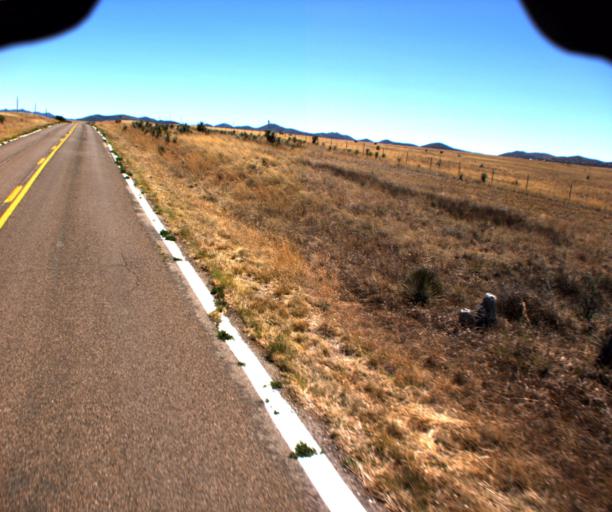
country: US
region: Arizona
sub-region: Cochise County
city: Huachuca City
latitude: 31.6310
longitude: -110.5953
